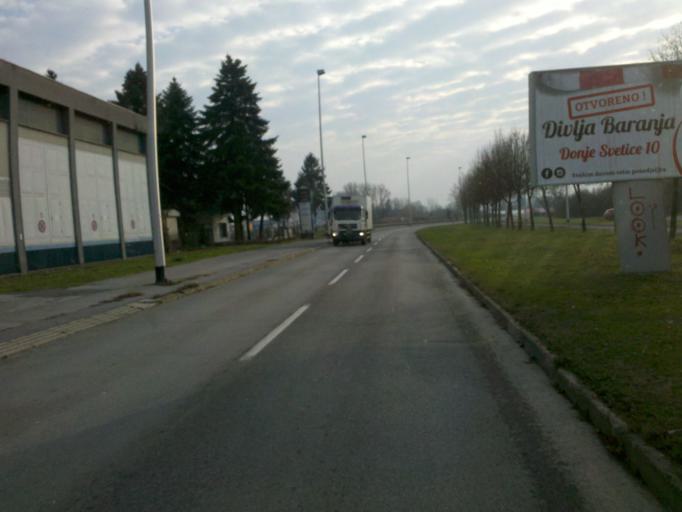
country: HR
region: Grad Zagreb
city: Dubrava
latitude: 45.7950
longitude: 16.0386
